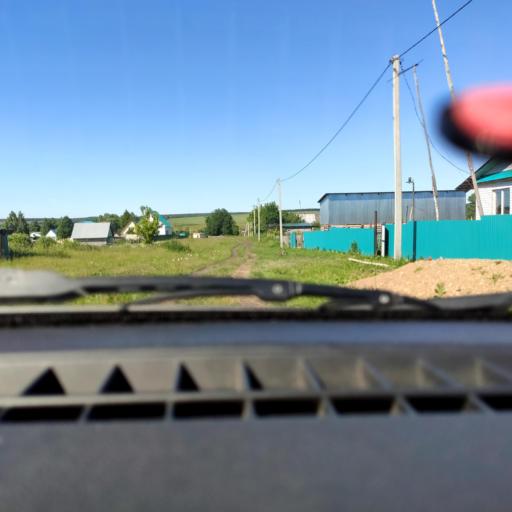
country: RU
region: Bashkortostan
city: Iglino
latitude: 54.8898
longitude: 56.4986
